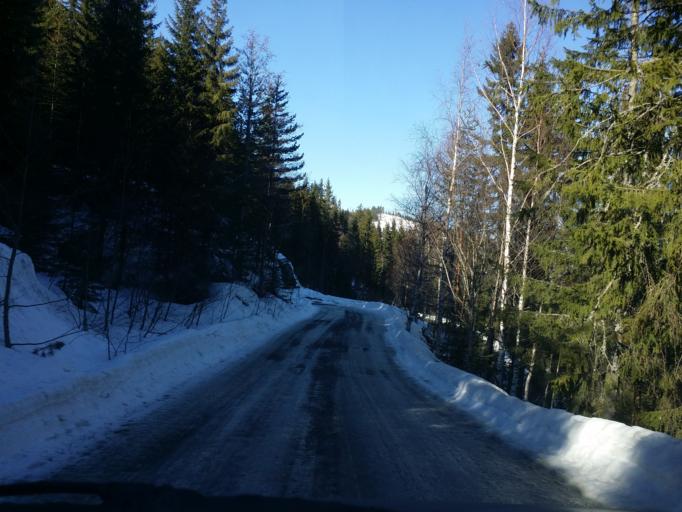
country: NO
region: Buskerud
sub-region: Ringerike
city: Honefoss
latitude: 60.3984
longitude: 10.0359
